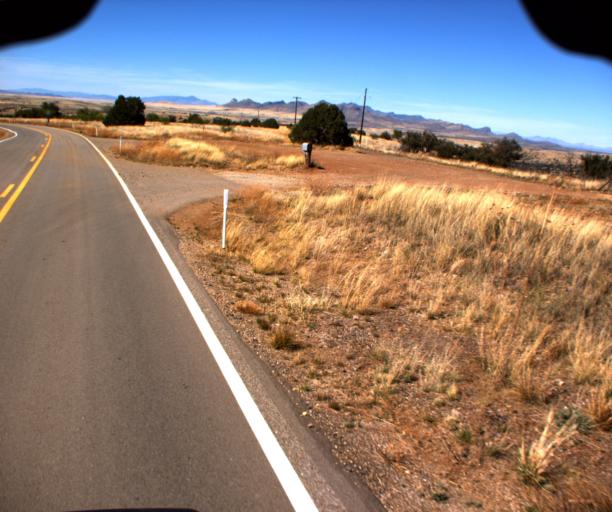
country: US
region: Arizona
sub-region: Cochise County
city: Huachuca City
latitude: 31.5348
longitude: -110.5025
